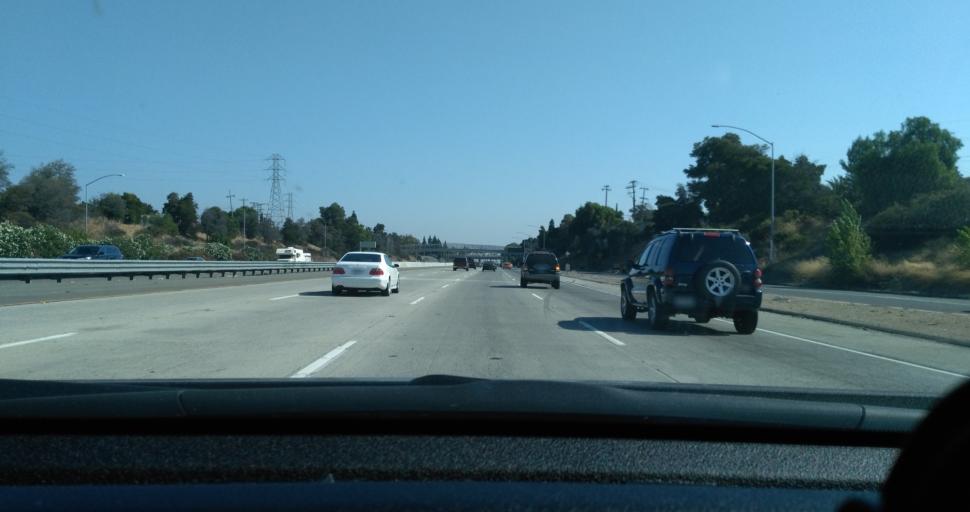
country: US
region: California
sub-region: Santa Clara County
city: Alum Rock
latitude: 37.3667
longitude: -121.8454
